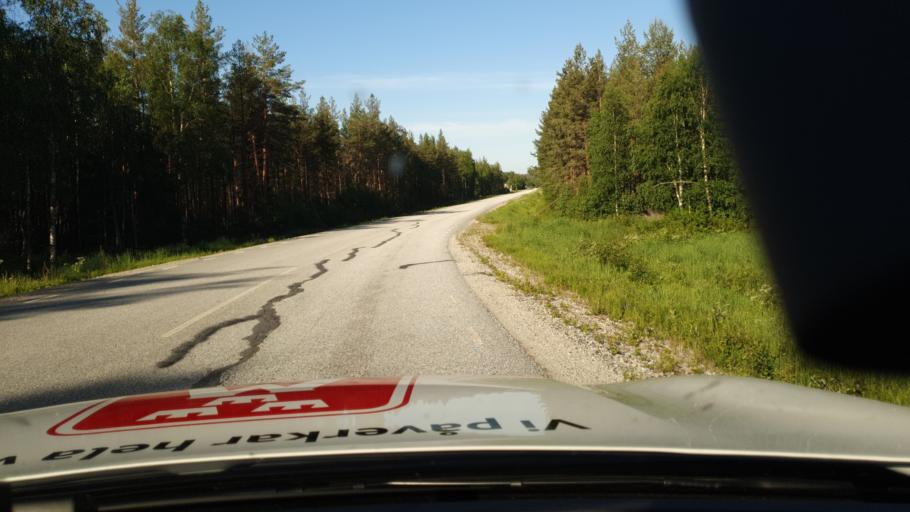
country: SE
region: Vaesterbotten
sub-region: Bjurholms Kommun
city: Bjurholm
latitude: 64.1487
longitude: 19.3460
